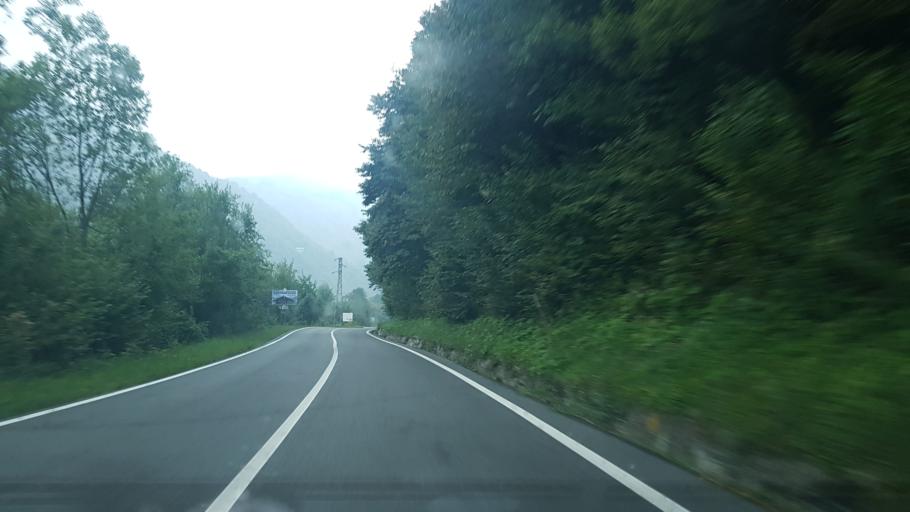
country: IT
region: Piedmont
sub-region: Provincia di Cuneo
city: Frabosa Sottana
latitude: 44.2802
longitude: 7.7685
